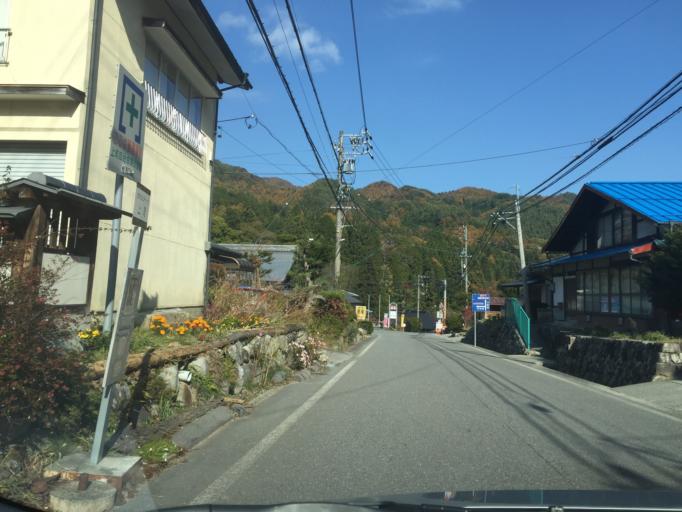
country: JP
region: Nagano
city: Iida
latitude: 35.3747
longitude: 137.6881
